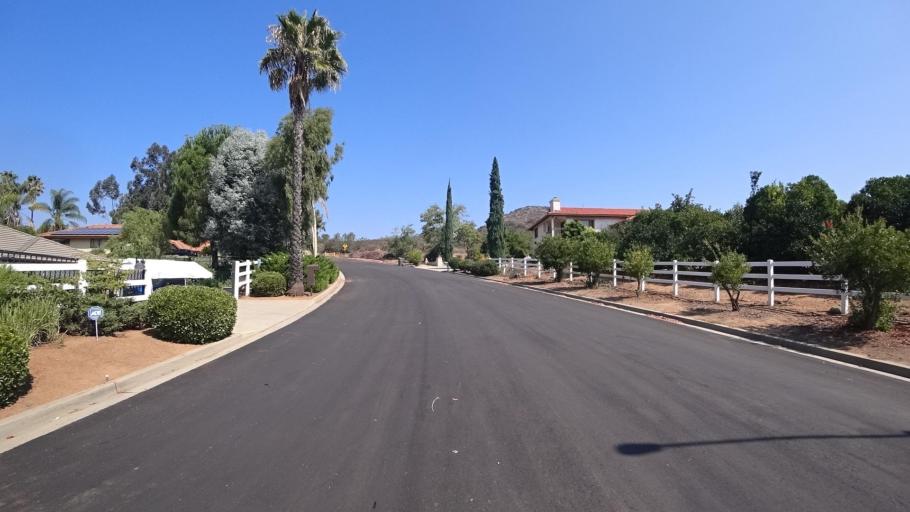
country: US
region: California
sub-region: San Diego County
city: Bonsall
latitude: 33.2558
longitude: -117.1909
